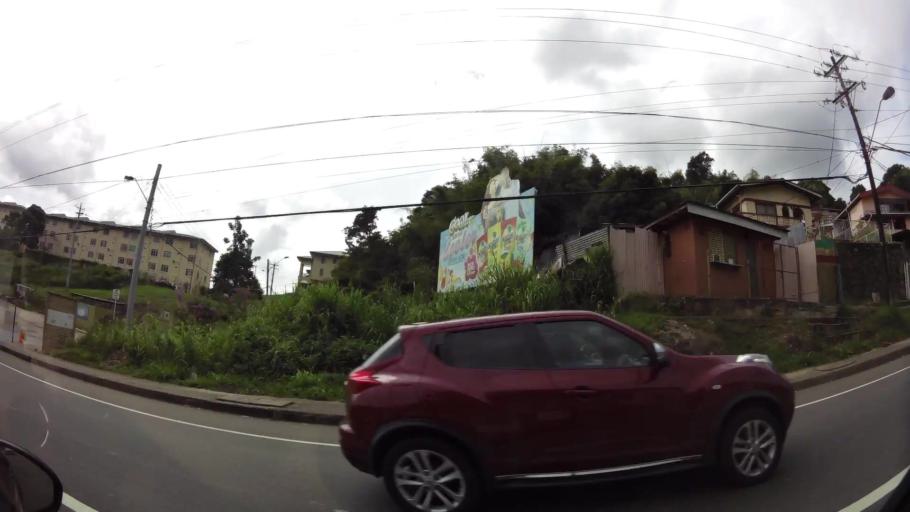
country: TT
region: San Juan/Laventille
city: Laventille
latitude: 10.6684
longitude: -61.4881
